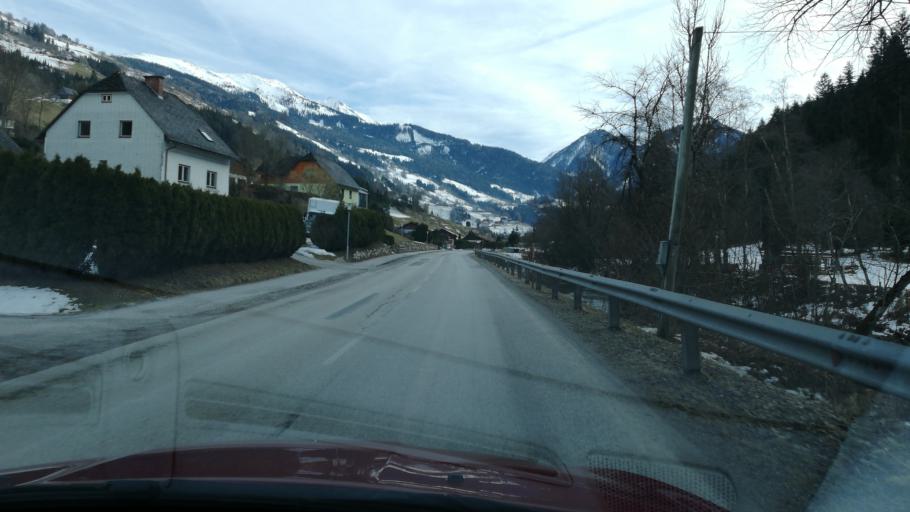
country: AT
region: Styria
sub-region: Politischer Bezirk Liezen
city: Donnersbach
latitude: 47.4747
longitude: 14.1196
